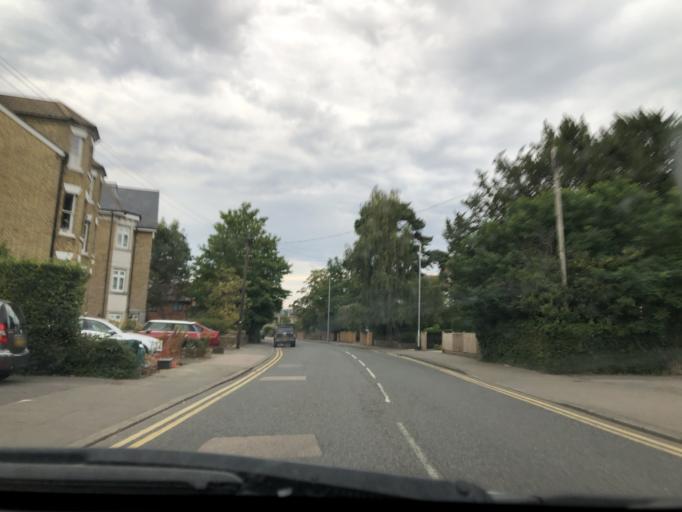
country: GB
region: England
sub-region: Kent
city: Sevenoaks
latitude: 51.2783
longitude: 0.1939
